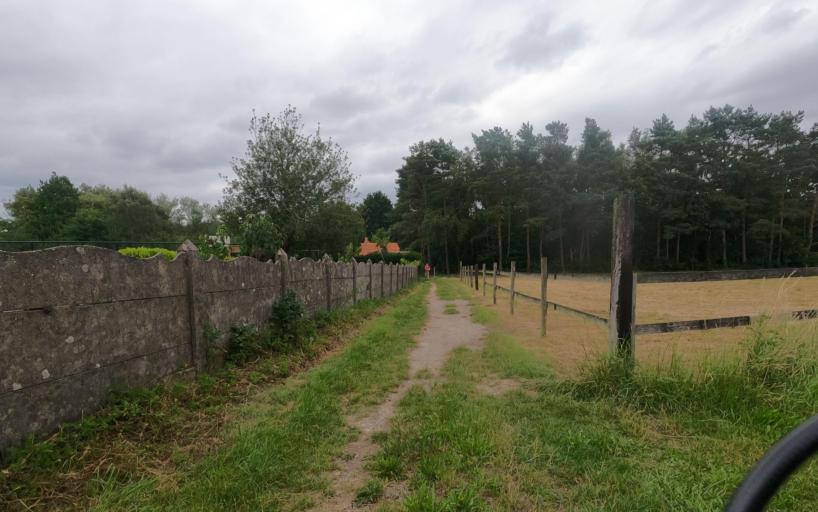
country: BE
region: Flanders
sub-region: Provincie Vlaams-Brabant
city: Tremelo
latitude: 50.9786
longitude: 4.7384
